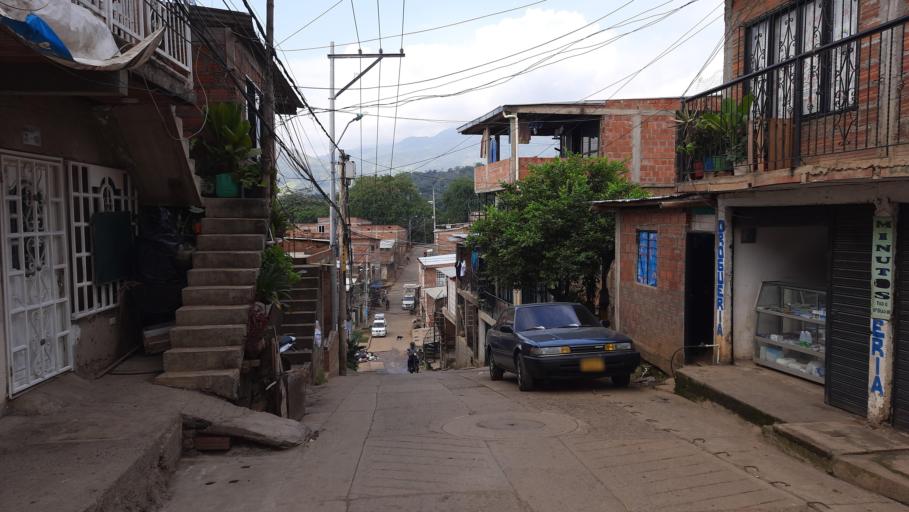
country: CO
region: Valle del Cauca
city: Cali
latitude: 3.3768
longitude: -76.5585
